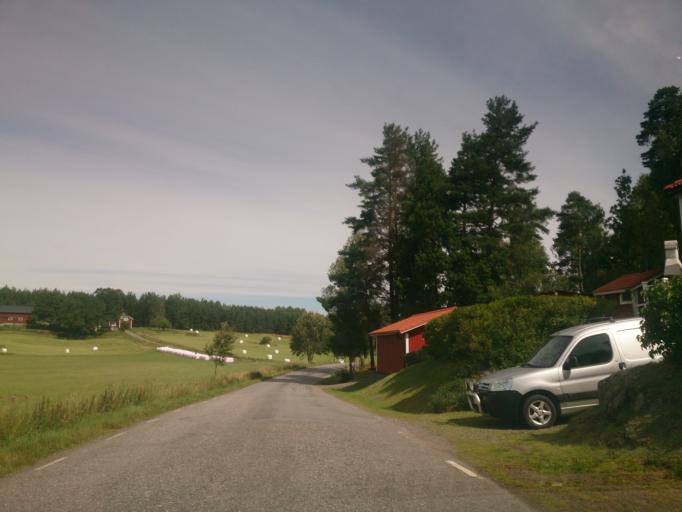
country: SE
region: OEstergoetland
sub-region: Valdemarsviks Kommun
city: Gusum
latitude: 58.2916
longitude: 16.5337
